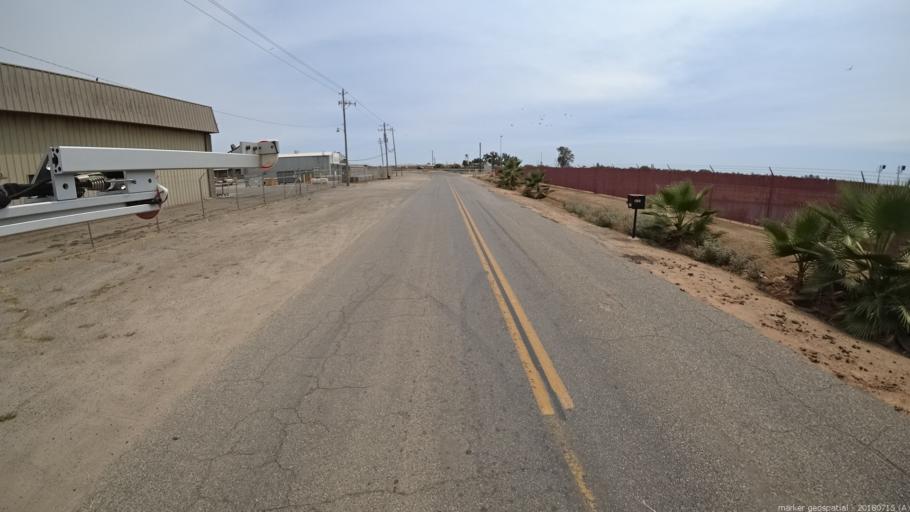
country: US
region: California
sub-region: Madera County
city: Madera Acres
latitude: 37.0061
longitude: -120.1106
